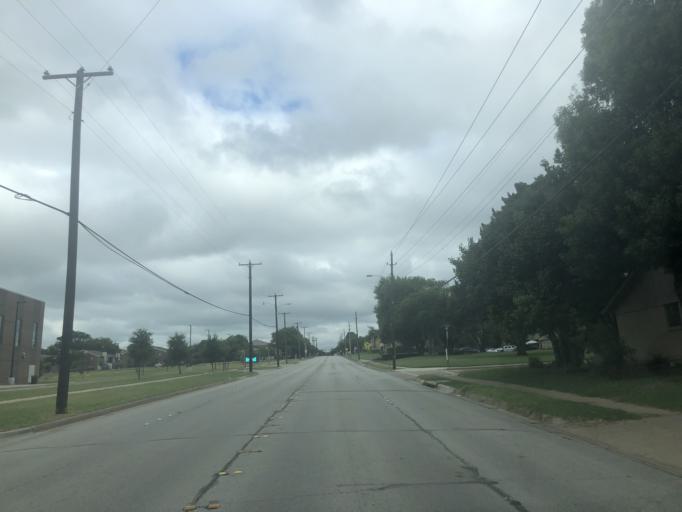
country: US
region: Texas
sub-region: Dallas County
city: Duncanville
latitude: 32.6517
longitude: -96.9209
